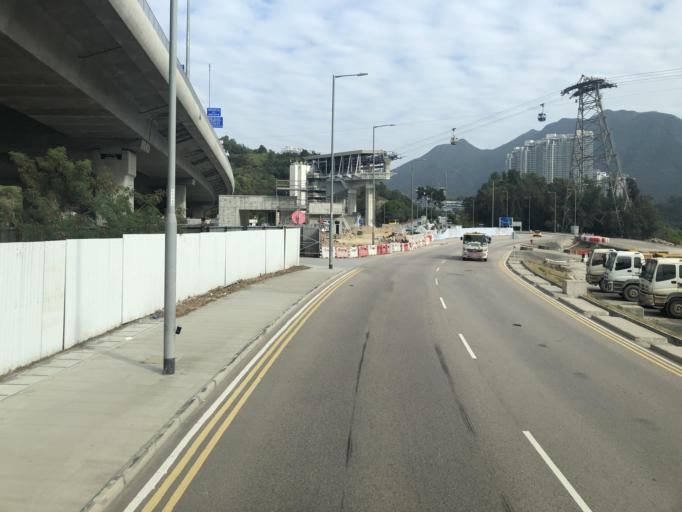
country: HK
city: Tai O
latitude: 22.2917
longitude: 113.9300
